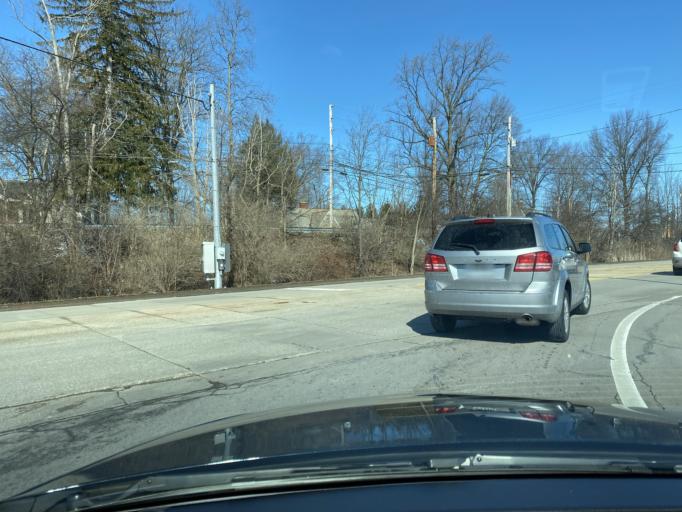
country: US
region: Ohio
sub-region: Summit County
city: Fairlawn
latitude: 41.1201
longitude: -81.6386
